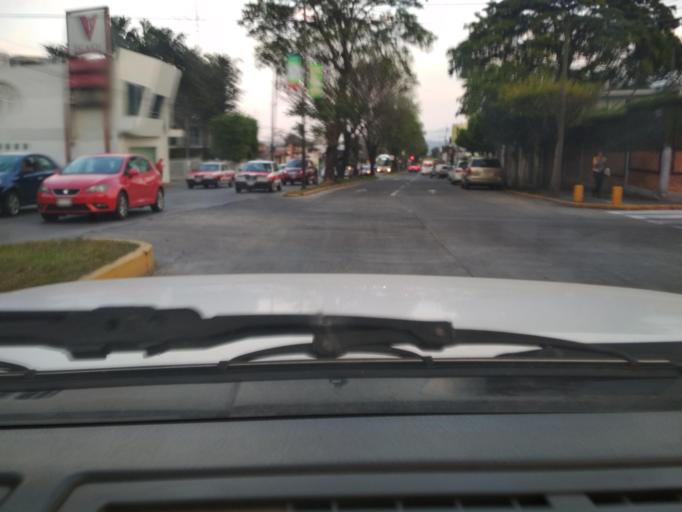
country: MX
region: Veracruz
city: Orizaba
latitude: 18.8584
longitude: -97.0906
